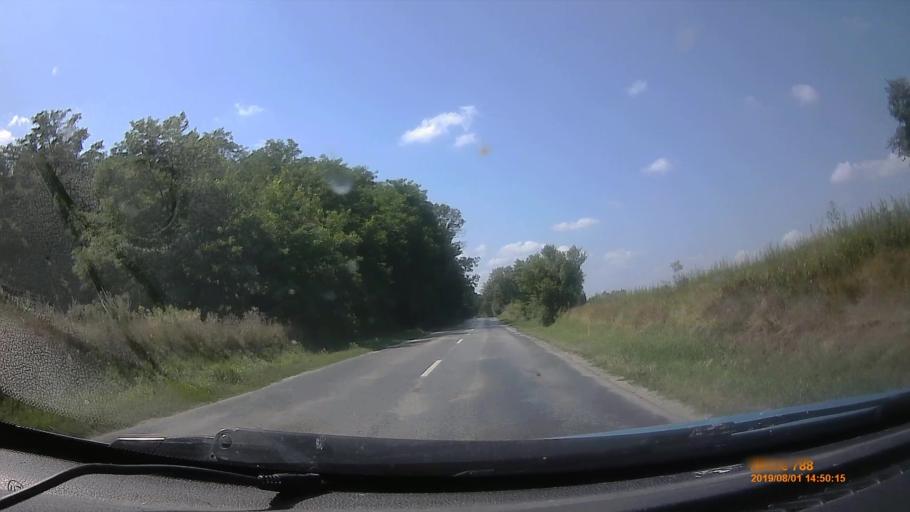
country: HU
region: Baranya
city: Vajszlo
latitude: 45.8512
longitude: 18.0081
